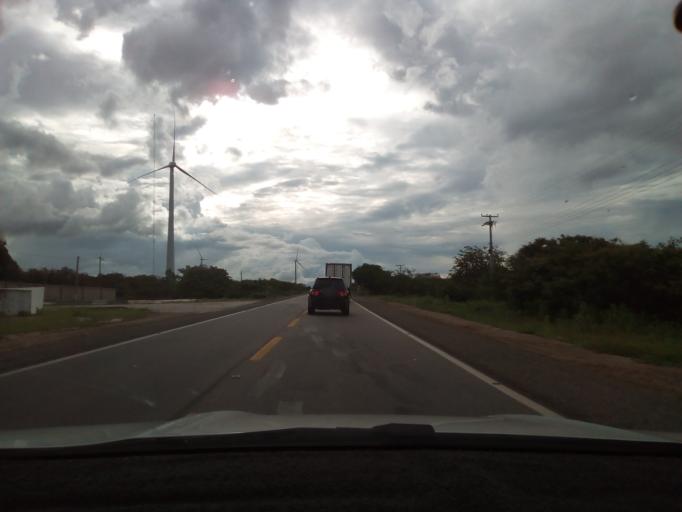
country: BR
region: Ceara
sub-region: Aracati
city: Aracati
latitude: -4.5878
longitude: -37.7006
